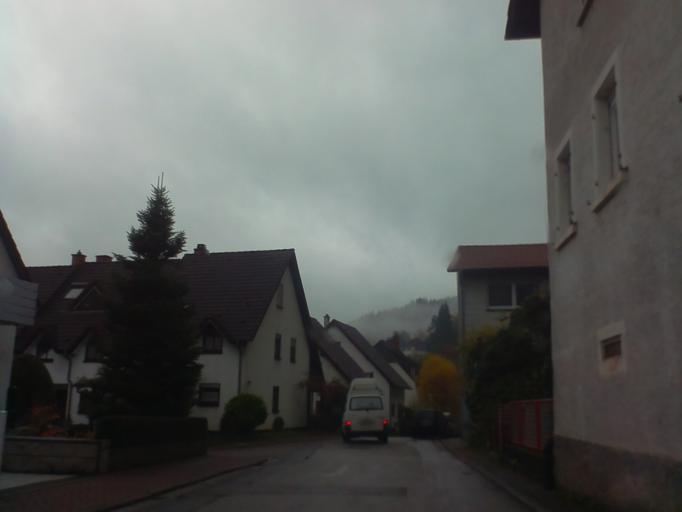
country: DE
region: Baden-Wuerttemberg
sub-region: Karlsruhe Region
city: Schonau
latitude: 49.4380
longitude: 8.8090
